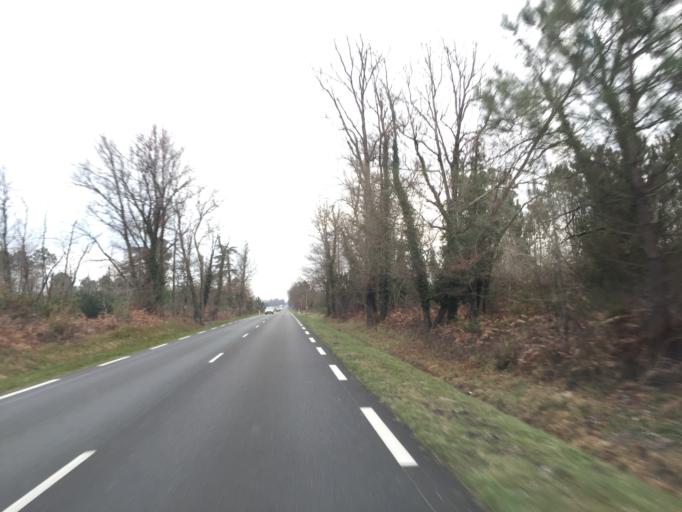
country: FR
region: Aquitaine
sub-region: Departement de la Gironde
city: Saint-Sauveur
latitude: 45.1935
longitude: -0.8535
